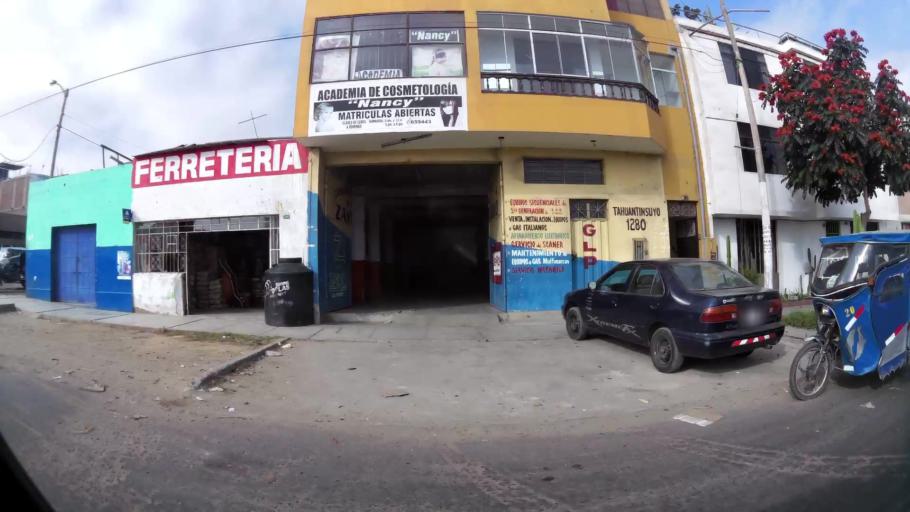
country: PE
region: La Libertad
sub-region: Provincia de Trujillo
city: La Esperanza
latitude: -8.0803
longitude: -79.0444
